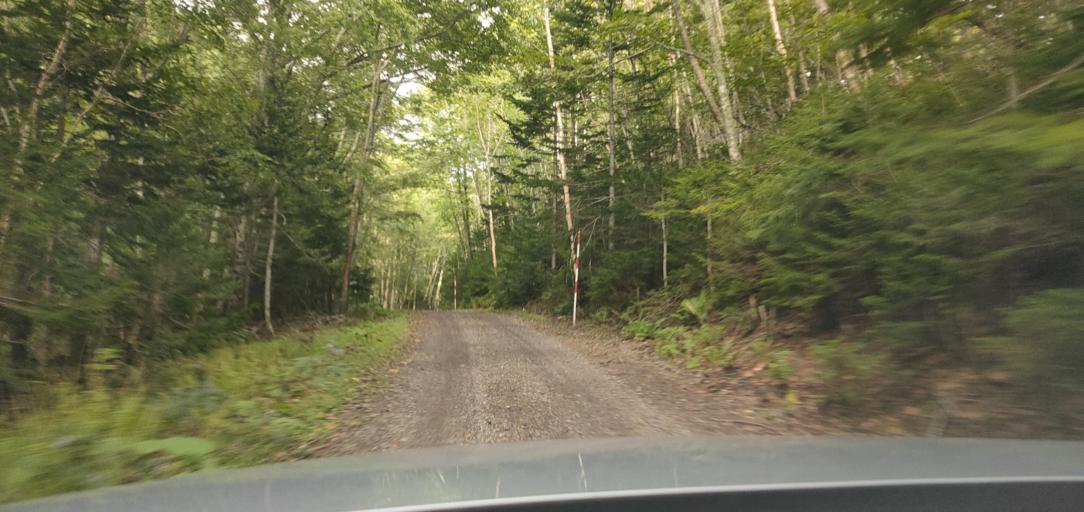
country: JP
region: Hokkaido
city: Kitami
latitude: 43.3706
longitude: 143.9547
